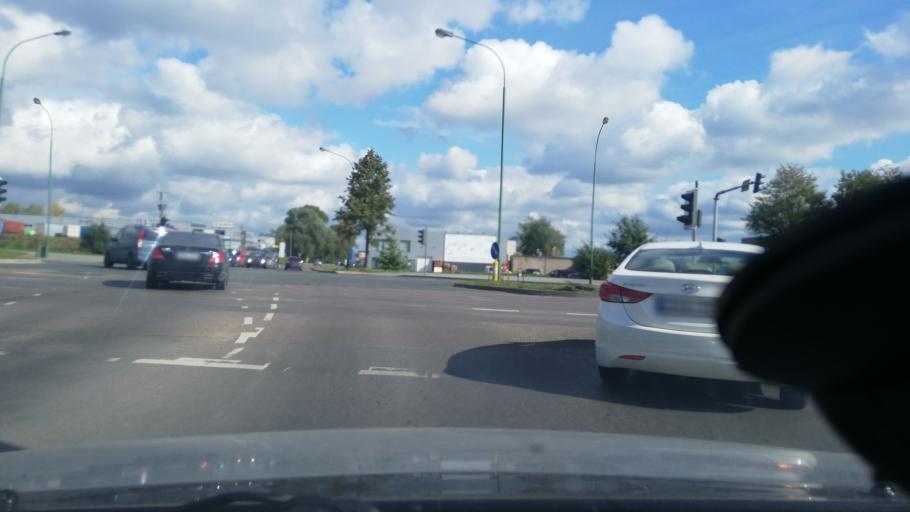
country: LT
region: Klaipedos apskritis
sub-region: Klaipeda
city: Klaipeda
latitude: 55.6857
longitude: 21.1830
